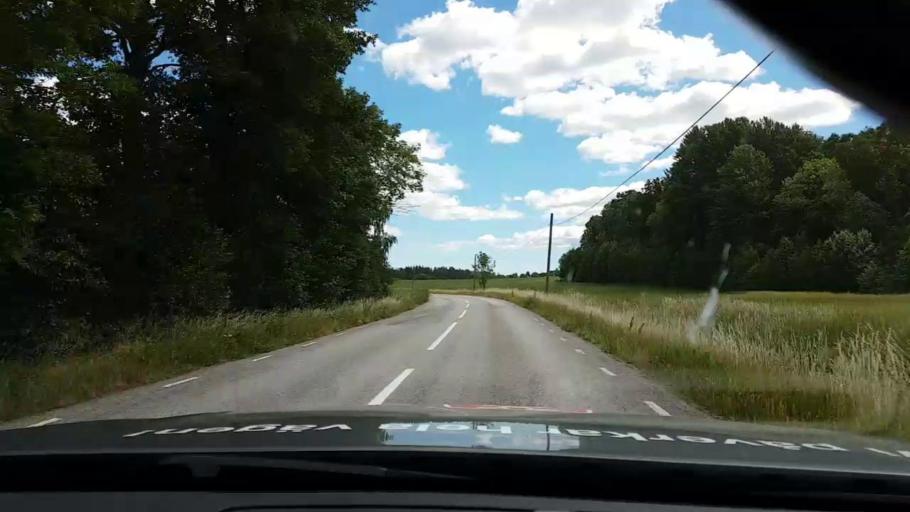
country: SE
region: Kalmar
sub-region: Vasterviks Kommun
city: Forserum
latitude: 58.0423
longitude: 16.4222
